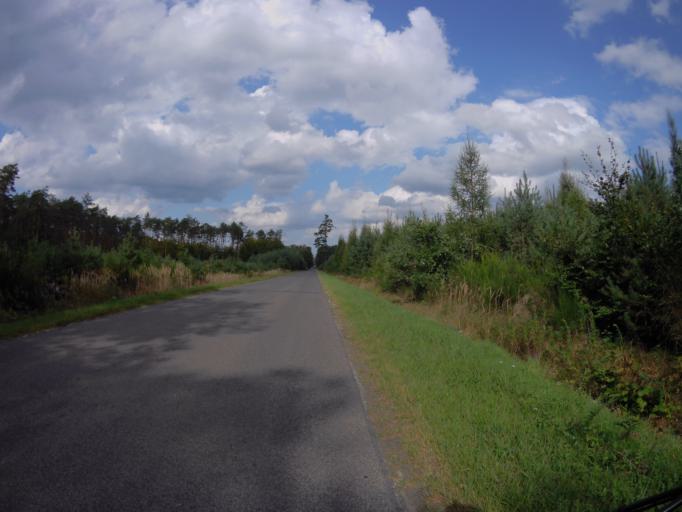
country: PL
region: Subcarpathian Voivodeship
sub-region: Powiat lezajski
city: Brzoza Krolewska
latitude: 50.2485
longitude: 22.3648
